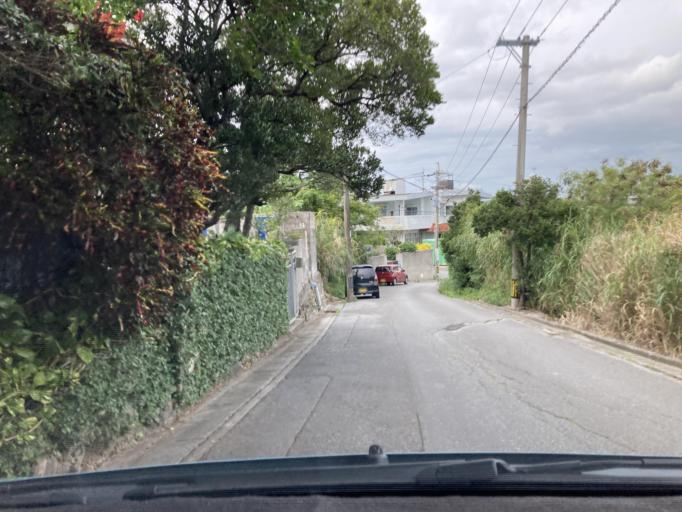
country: JP
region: Okinawa
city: Tomigusuku
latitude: 26.1755
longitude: 127.7147
